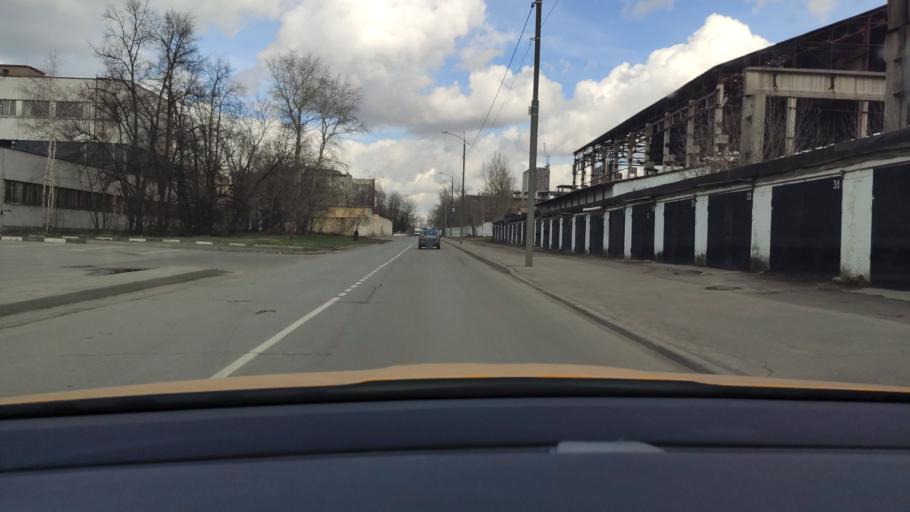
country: RU
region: Moscow
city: Ryazanskiy
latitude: 55.7184
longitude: 37.7645
